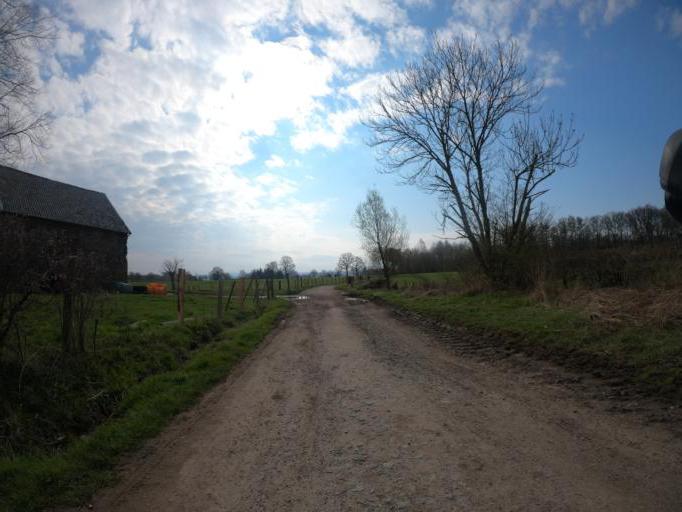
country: BE
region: Wallonia
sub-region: Province de Liege
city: Raeren
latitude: 50.7116
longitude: 6.1328
